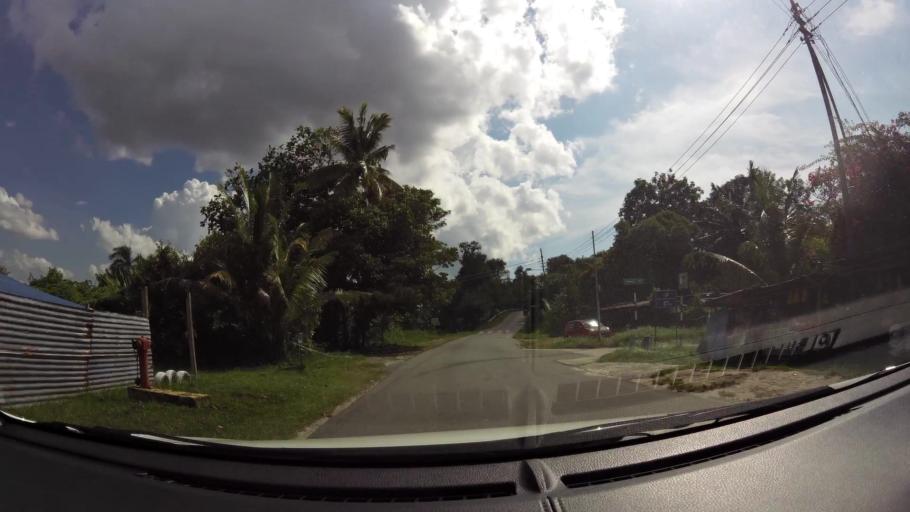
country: BN
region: Brunei and Muara
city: Bandar Seri Begawan
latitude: 4.9563
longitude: 114.9528
